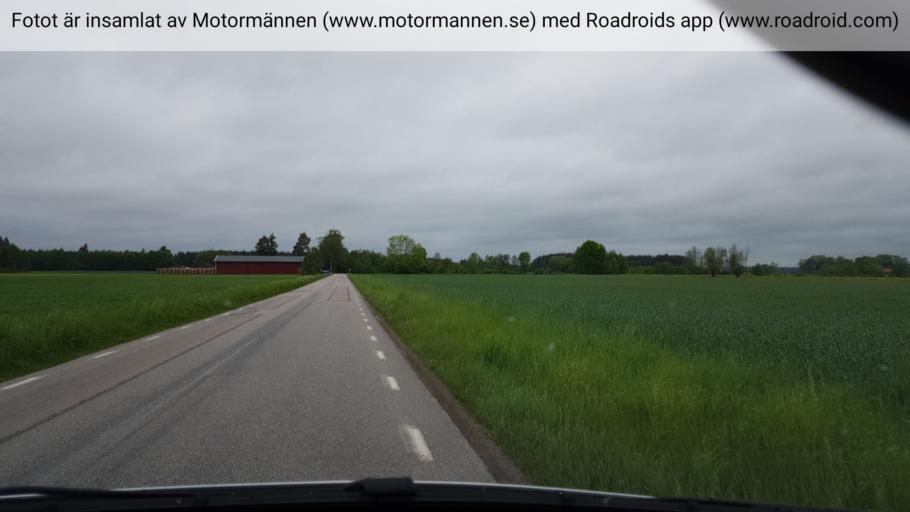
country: SE
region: Vaestra Goetaland
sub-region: Gotene Kommun
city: Kallby
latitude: 58.4767
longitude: 13.3227
